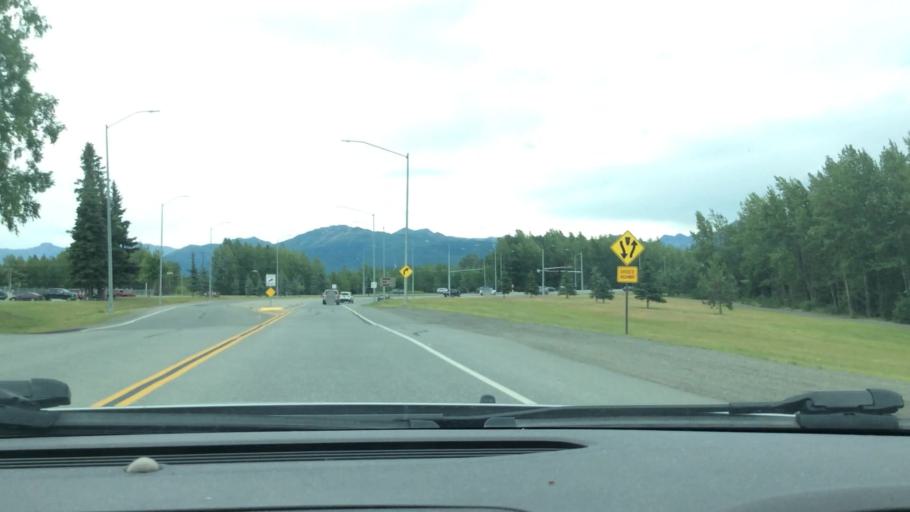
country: US
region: Alaska
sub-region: Anchorage Municipality
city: Anchorage
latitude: 61.2405
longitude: -149.7845
